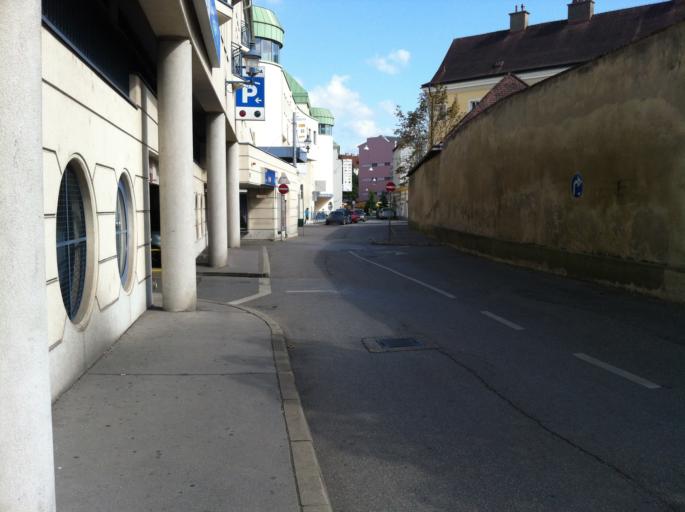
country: AT
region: Lower Austria
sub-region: Sankt Polten Stadt
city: Sankt Poelten
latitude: 48.2059
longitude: 15.6217
